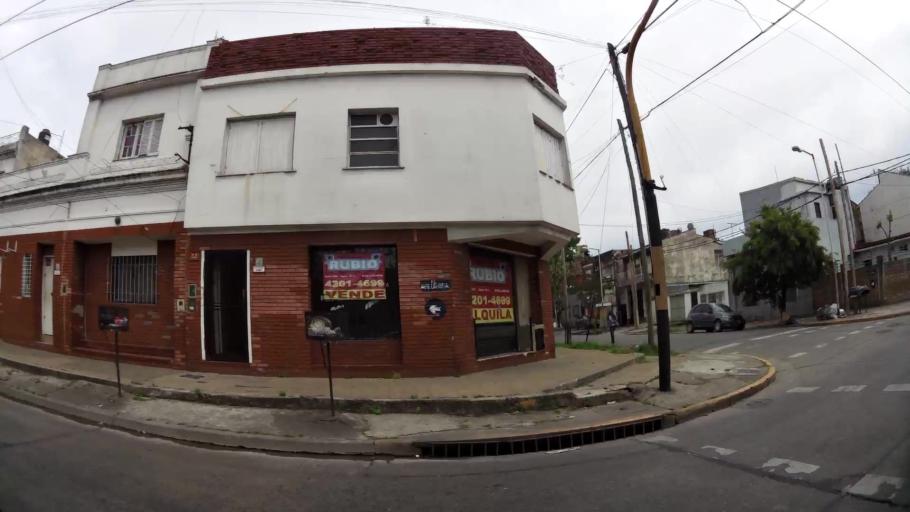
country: AR
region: Buenos Aires
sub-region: Partido de Avellaneda
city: Avellaneda
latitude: -34.6507
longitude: -58.3478
